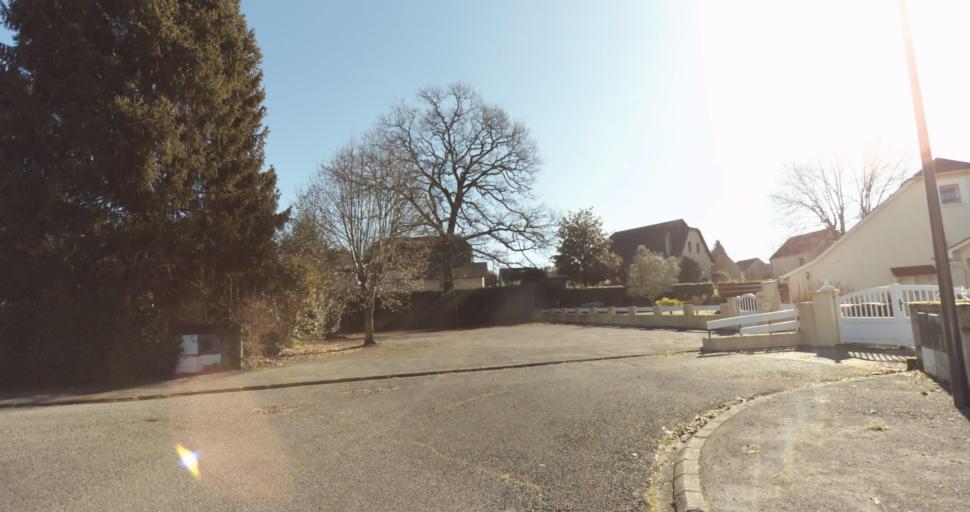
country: FR
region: Aquitaine
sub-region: Departement des Pyrenees-Atlantiques
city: Morlaas
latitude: 43.3482
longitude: -0.2638
